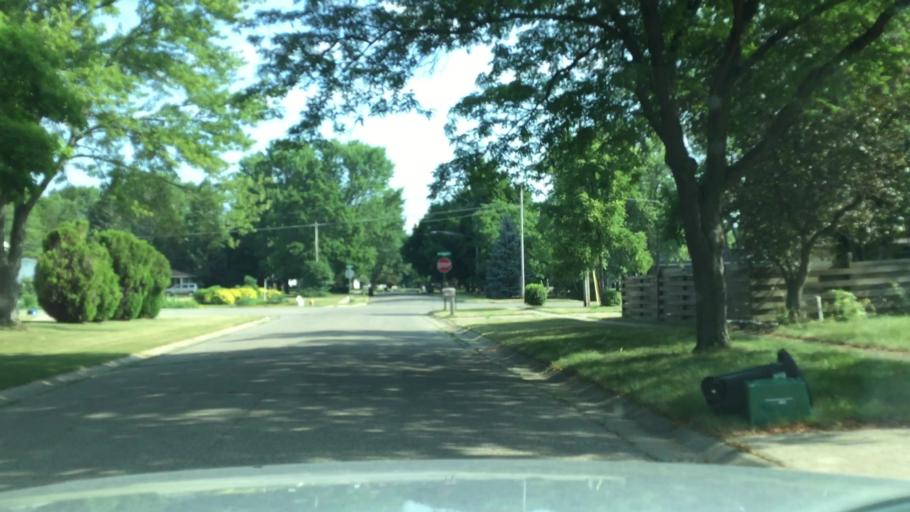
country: US
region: Michigan
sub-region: Genesee County
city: Flushing
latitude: 43.0591
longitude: -83.8650
